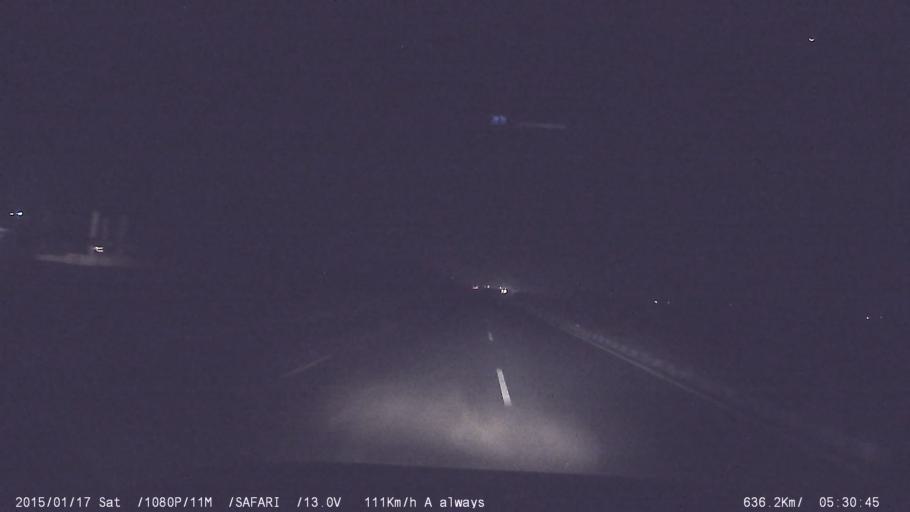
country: IN
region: Tamil Nadu
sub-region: Vellore
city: Arcot
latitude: 12.9122
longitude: 79.3048
